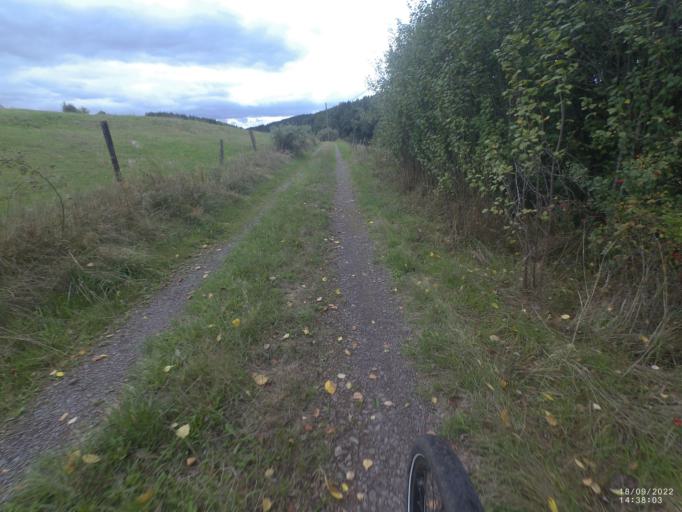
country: DE
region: Rheinland-Pfalz
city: Meisburg
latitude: 50.1060
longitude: 6.6888
